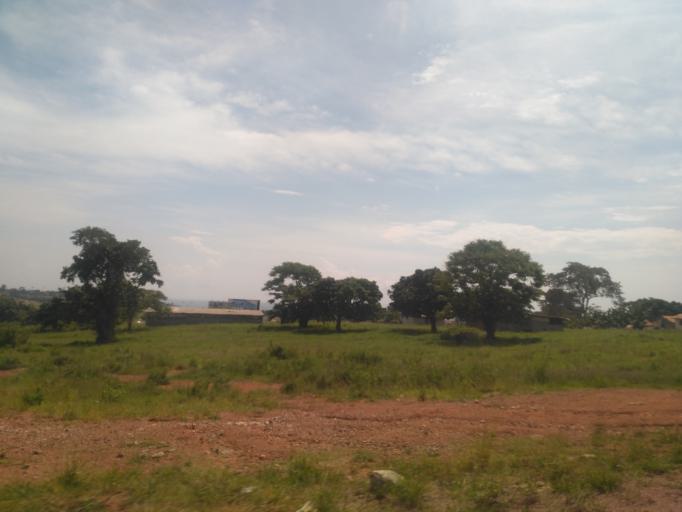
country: UG
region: Central Region
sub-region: Wakiso District
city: Entebbe
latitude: 0.0386
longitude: 32.4478
